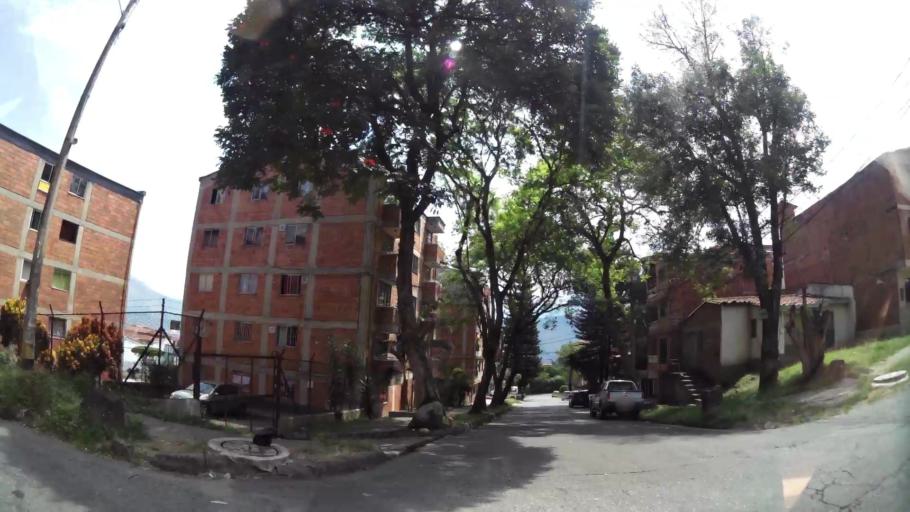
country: CO
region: Antioquia
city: Bello
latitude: 6.3181
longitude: -75.5660
